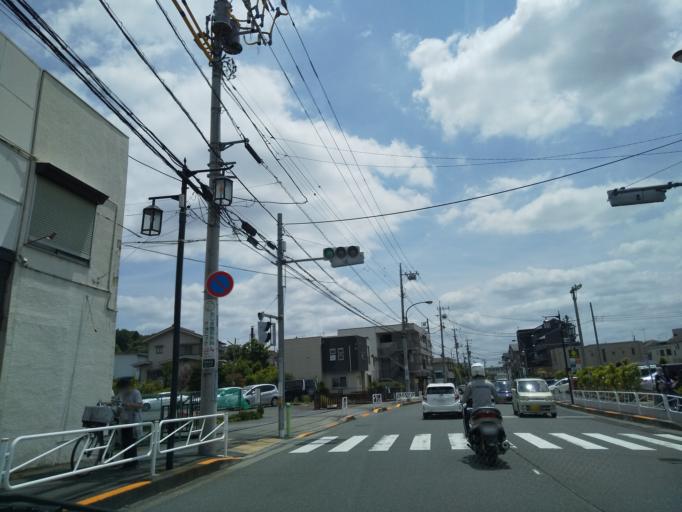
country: JP
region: Tokyo
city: Hachioji
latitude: 35.6732
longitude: 139.3294
